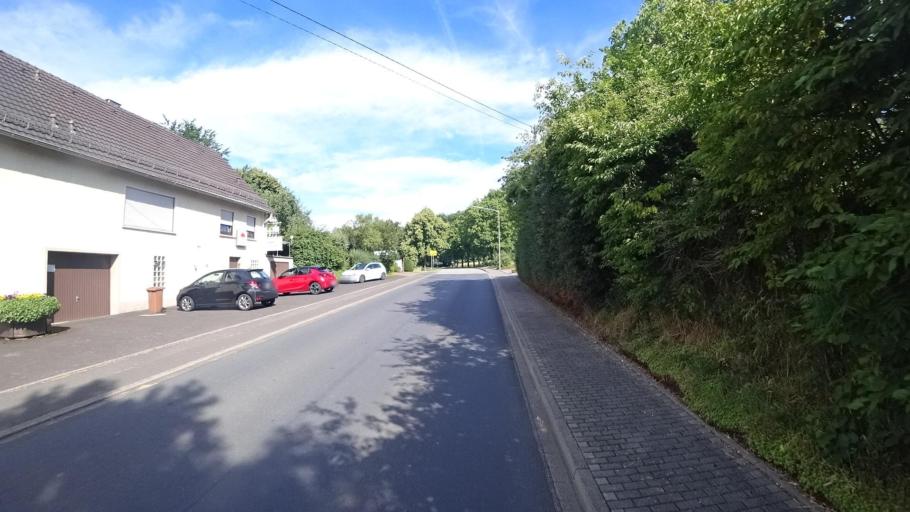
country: DE
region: Rheinland-Pfalz
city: Oberwambach
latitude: 50.6598
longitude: 7.6530
